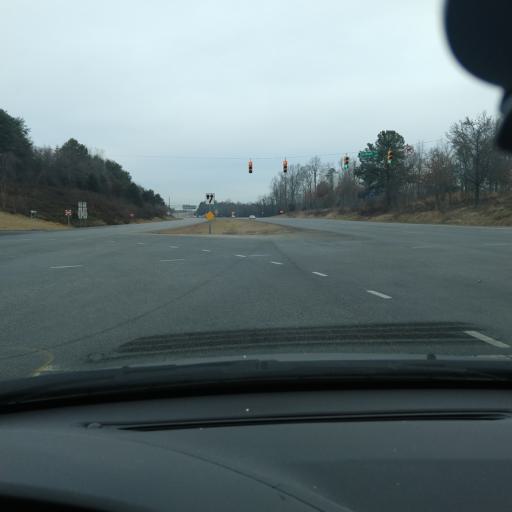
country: US
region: North Carolina
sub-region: Guilford County
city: Jamestown
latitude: 36.0814
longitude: -79.9598
